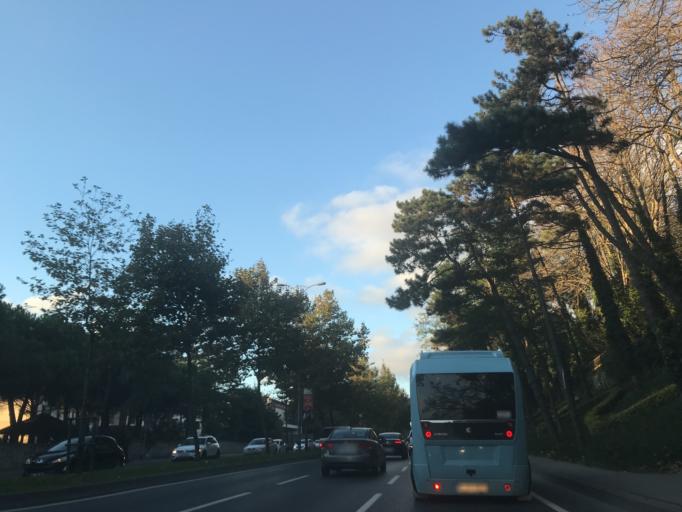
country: TR
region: Istanbul
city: Sisli
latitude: 41.1310
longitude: 29.0245
